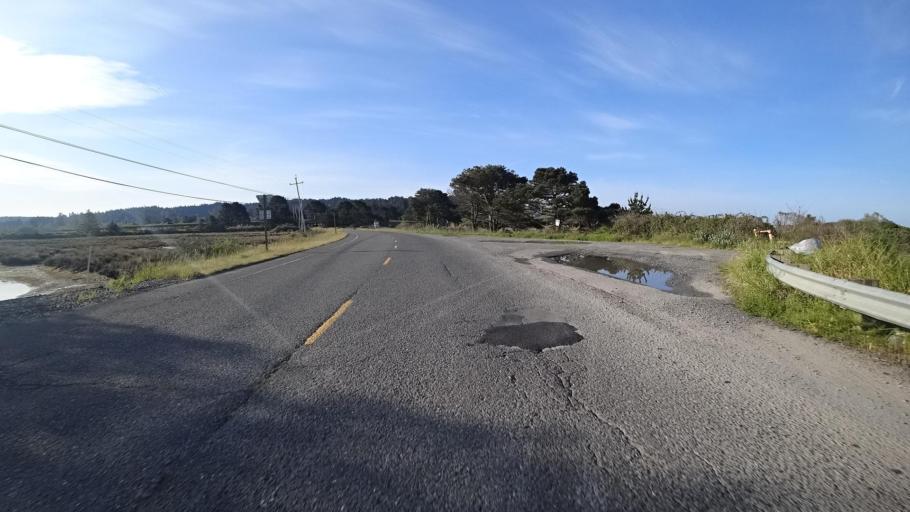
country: US
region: California
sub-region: Humboldt County
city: Humboldt Hill
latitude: 40.7384
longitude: -124.2122
